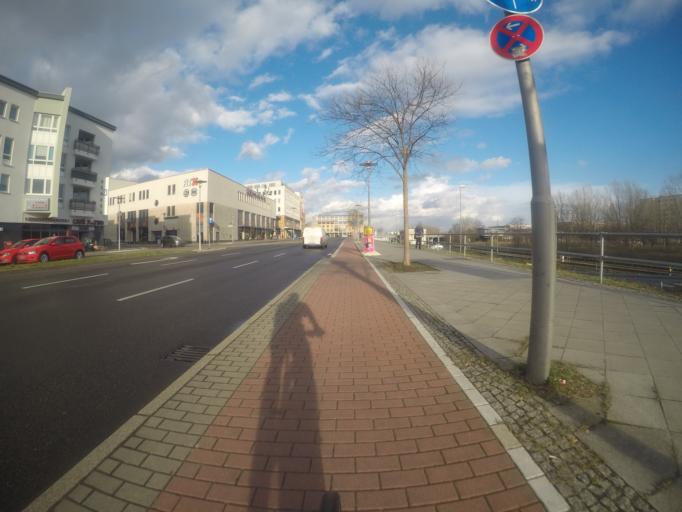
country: DE
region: Berlin
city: Hellersdorf
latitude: 52.5357
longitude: 13.6018
